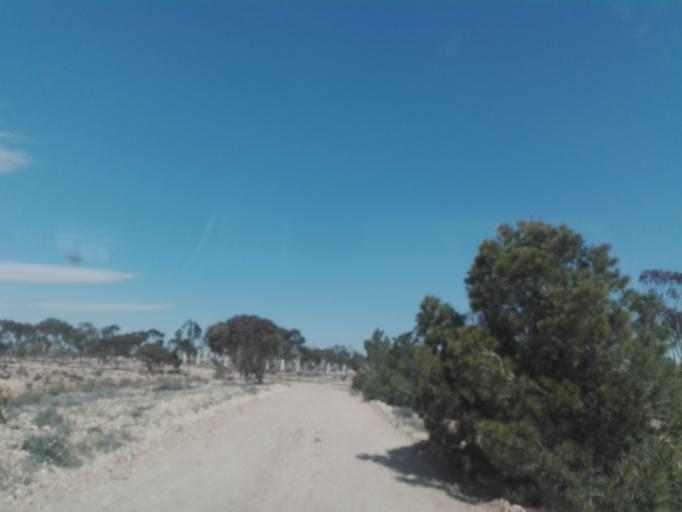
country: TN
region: Safaqis
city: Sfax
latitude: 34.7020
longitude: 10.5289
